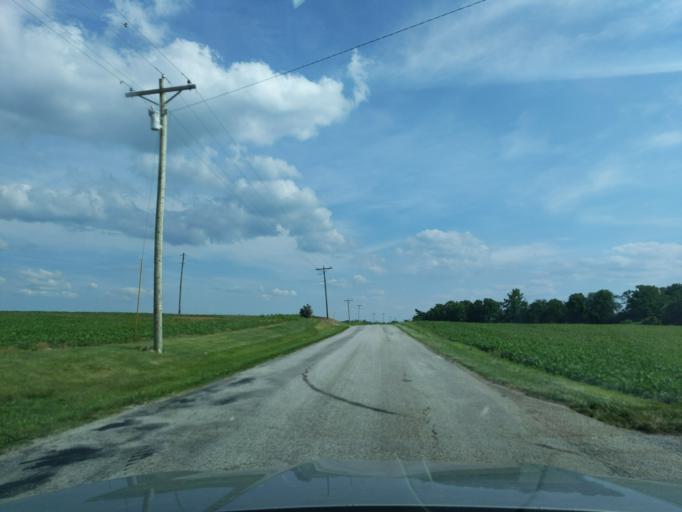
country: US
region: Indiana
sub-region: Decatur County
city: Greensburg
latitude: 39.2839
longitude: -85.4661
